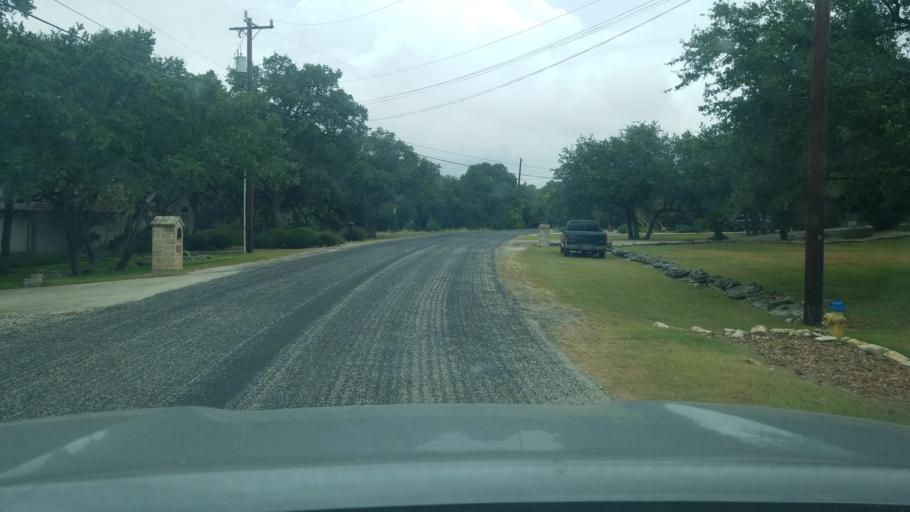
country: US
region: Texas
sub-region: Bexar County
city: Timberwood Park
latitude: 29.7050
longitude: -98.5115
